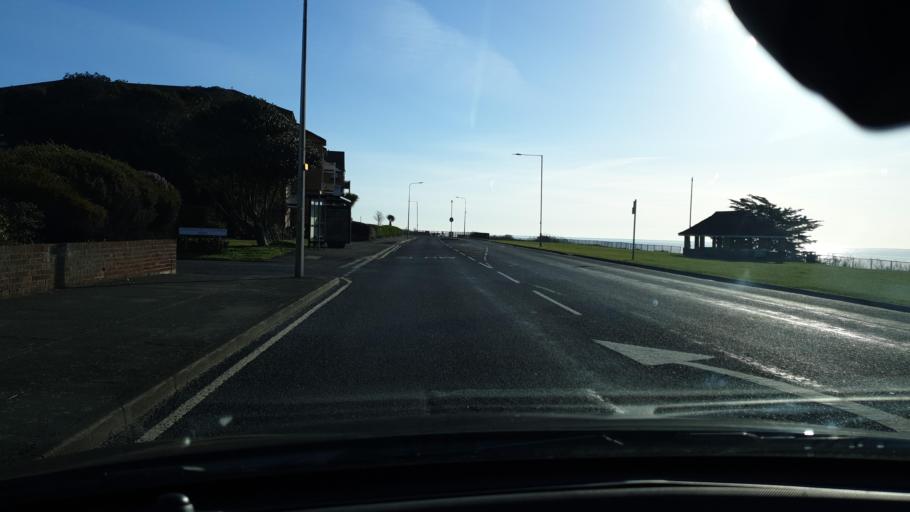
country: GB
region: England
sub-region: Essex
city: Clacton-on-Sea
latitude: 51.7938
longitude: 1.1705
